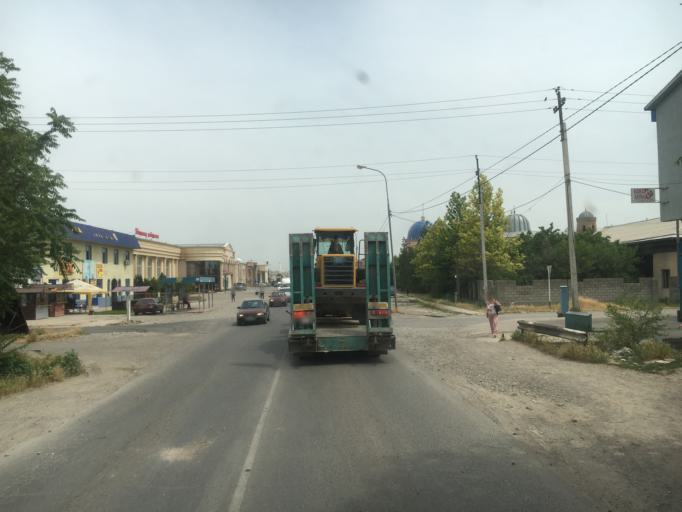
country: KZ
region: Ongtustik Qazaqstan
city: Shymkent
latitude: 42.3441
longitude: 69.5246
